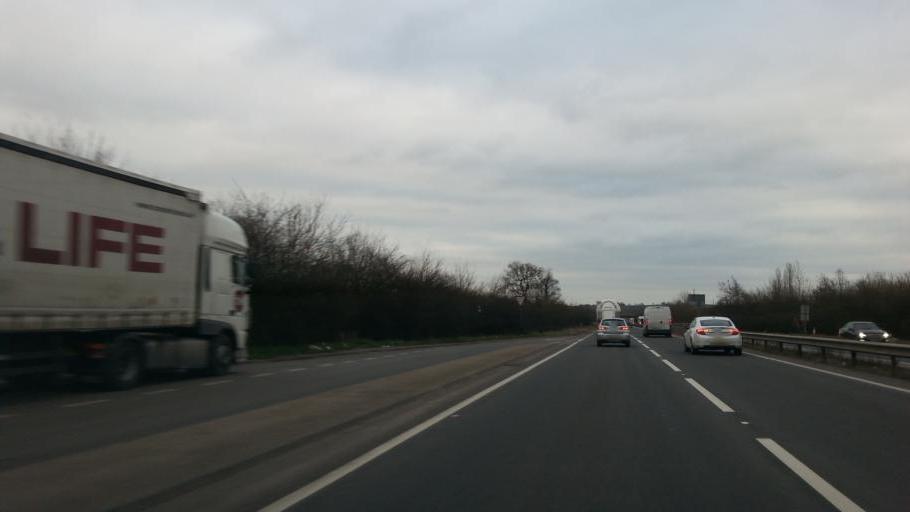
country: GB
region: England
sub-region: Northamptonshire
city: Long Buckby
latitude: 52.3935
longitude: -1.1176
